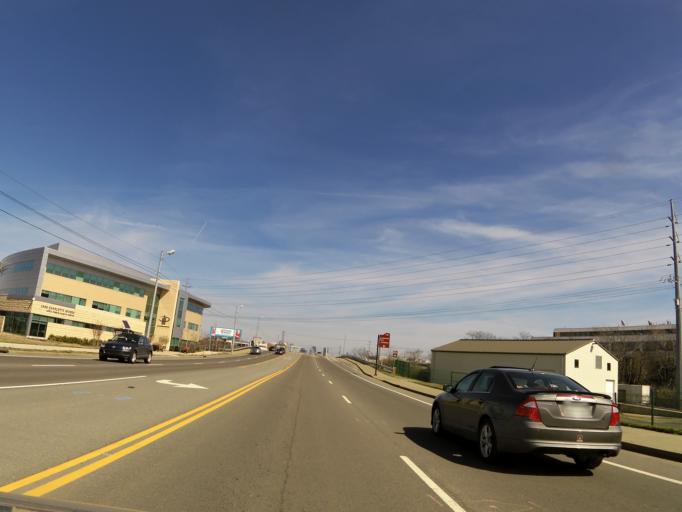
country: US
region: Tennessee
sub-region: Davidson County
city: Nashville
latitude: 36.1545
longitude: -86.8153
